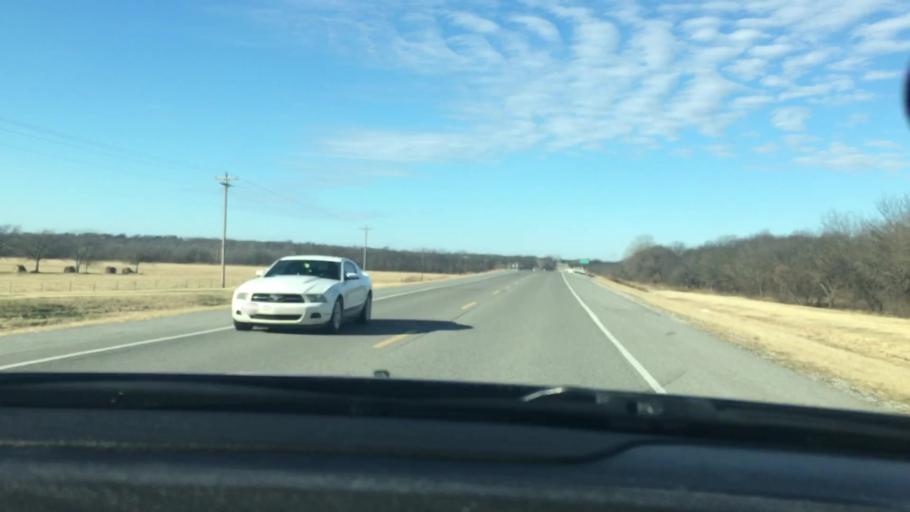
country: US
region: Oklahoma
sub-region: Love County
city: Marietta
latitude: 33.9403
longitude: -97.2943
